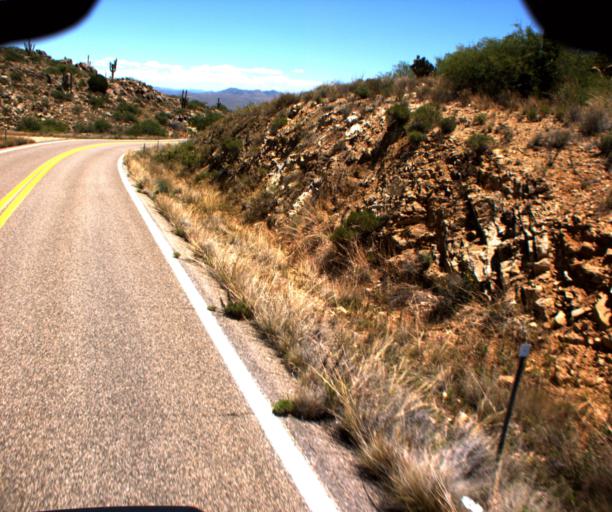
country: US
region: Arizona
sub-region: Yavapai County
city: Bagdad
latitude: 34.5258
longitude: -113.1295
